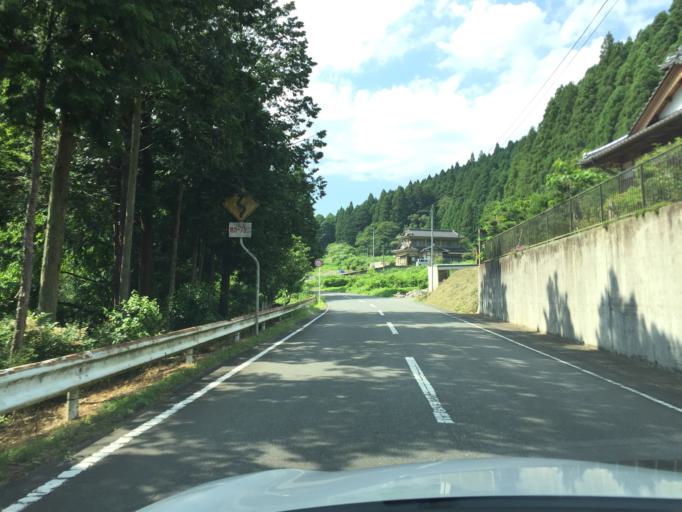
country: JP
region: Fukushima
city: Iwaki
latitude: 37.0222
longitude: 140.7053
